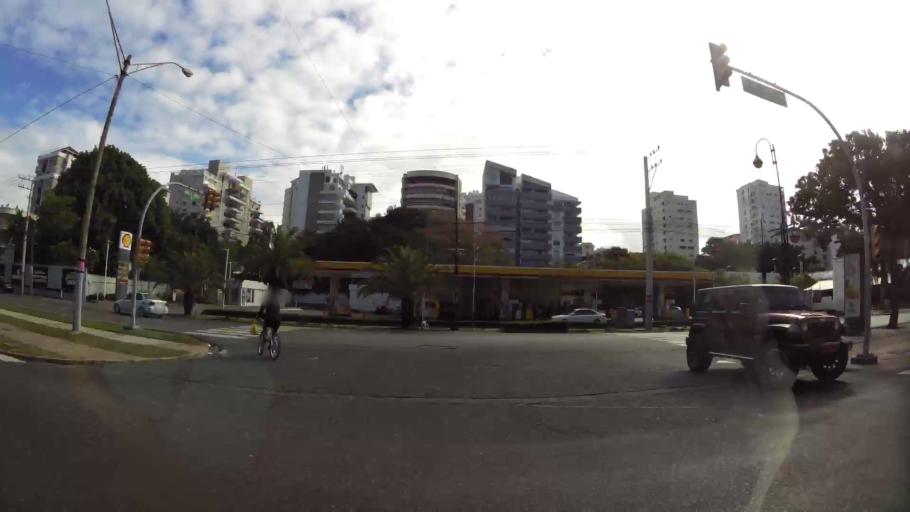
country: DO
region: Nacional
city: La Julia
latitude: 18.4742
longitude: -69.9426
